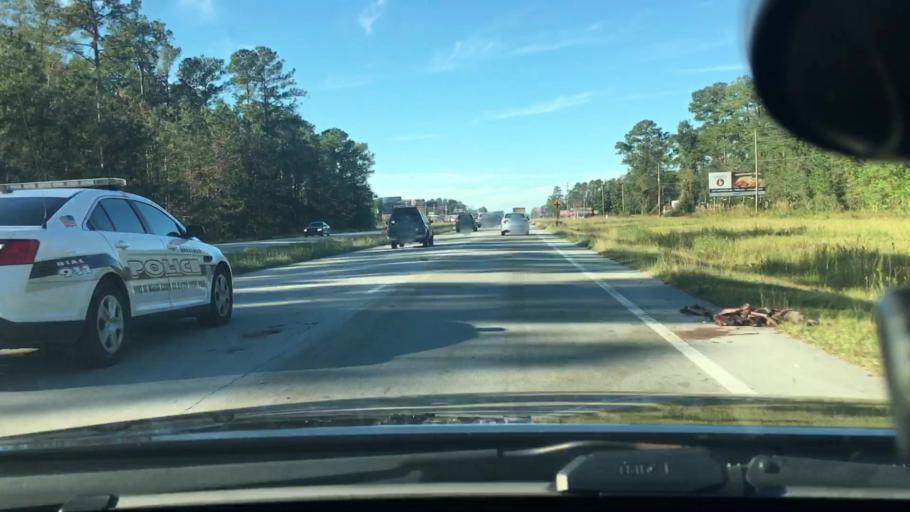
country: US
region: North Carolina
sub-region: Craven County
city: James City
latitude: 35.0537
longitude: -77.0162
